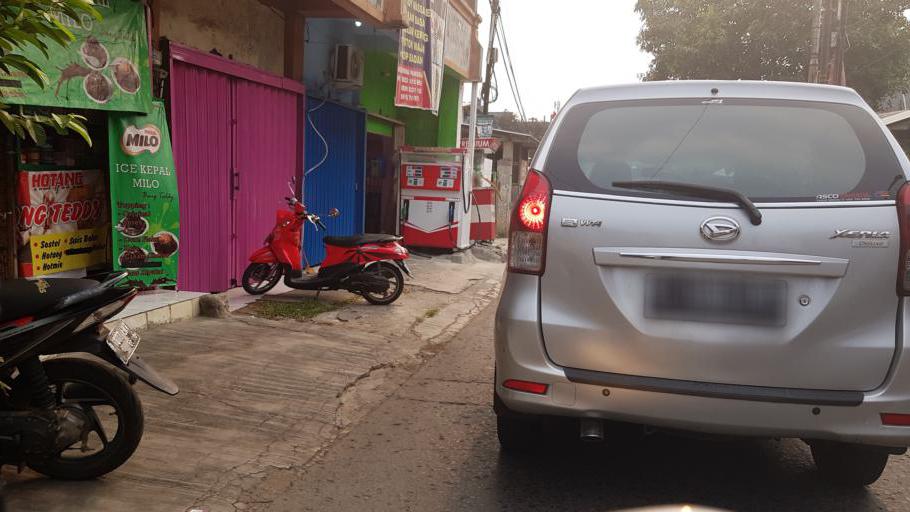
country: ID
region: West Java
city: Depok
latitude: -6.3723
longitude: 106.8504
